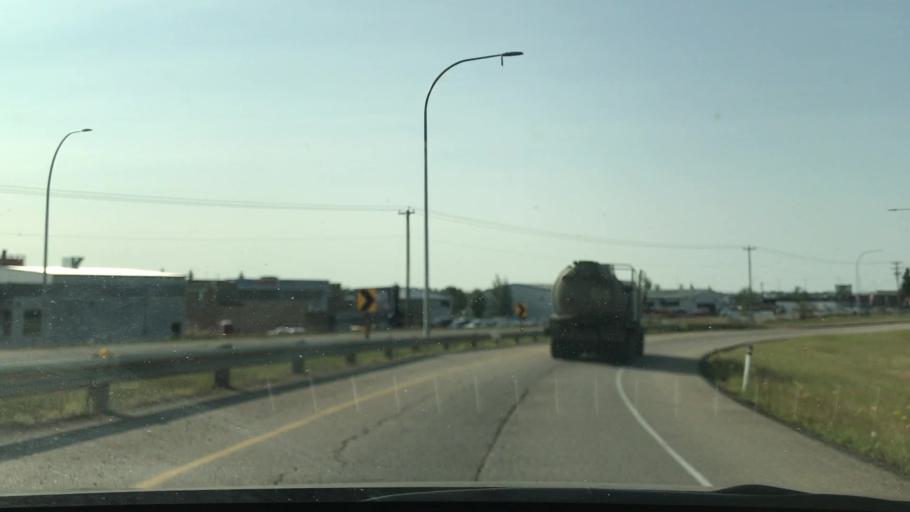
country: CA
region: Alberta
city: Leduc
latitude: 53.2833
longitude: -113.5478
